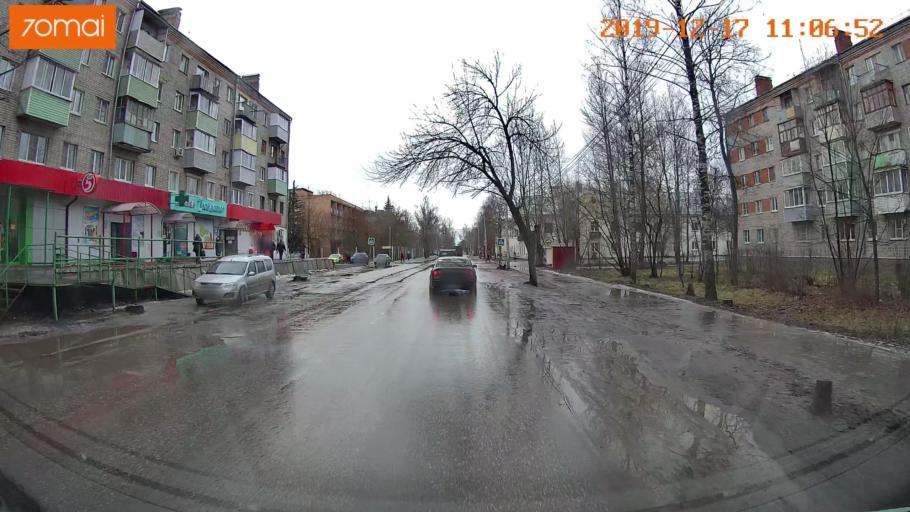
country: RU
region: Vladimir
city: Gus'-Khrustal'nyy
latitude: 55.6136
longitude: 40.6446
